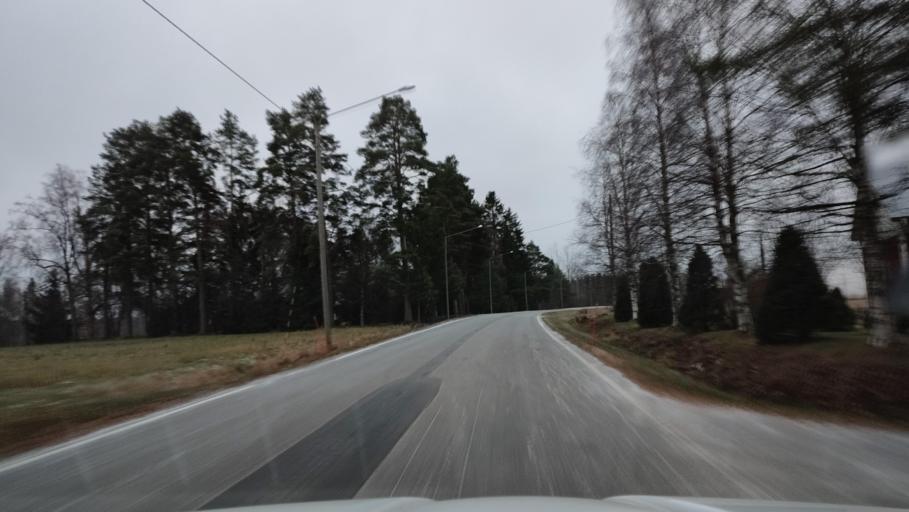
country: FI
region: Southern Ostrobothnia
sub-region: Suupohja
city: Karijoki
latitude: 62.2467
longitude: 21.6711
